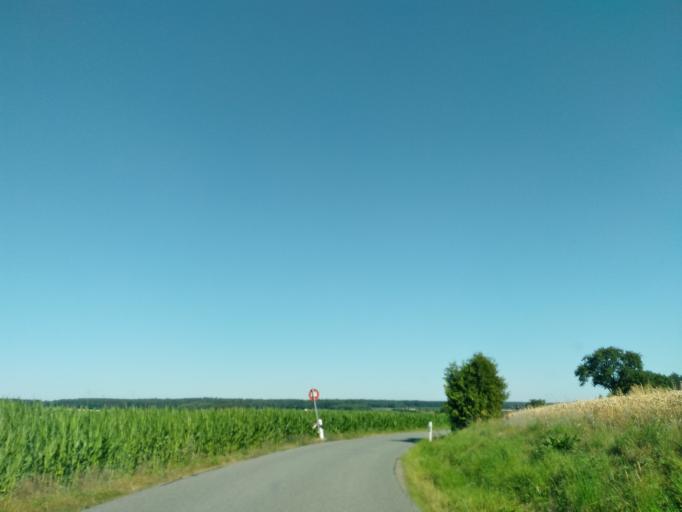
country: DE
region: Baden-Wuerttemberg
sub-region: Karlsruhe Region
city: Mudau
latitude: 49.5383
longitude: 9.2463
